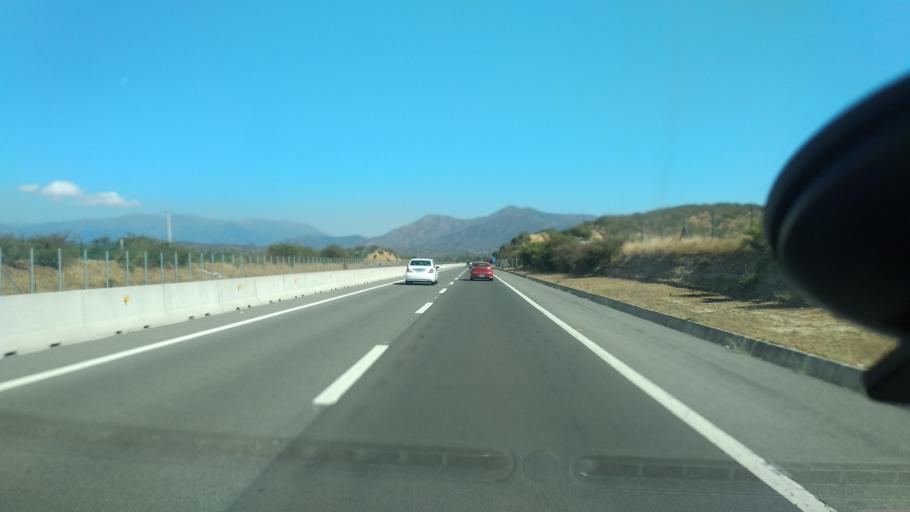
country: CL
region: Valparaiso
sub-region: Provincia de Marga Marga
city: Villa Alemana
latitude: -33.0078
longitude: -71.3267
